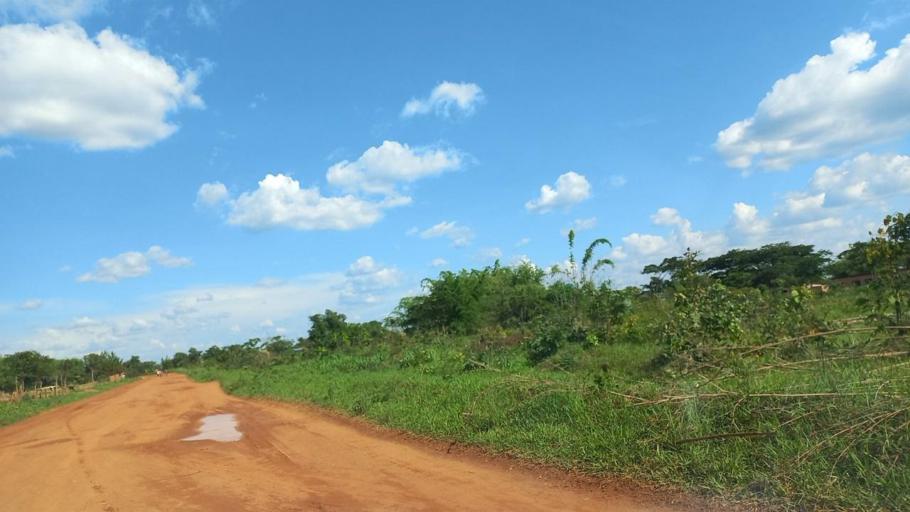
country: ZM
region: Copperbelt
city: Kitwe
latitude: -12.8701
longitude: 28.3581
